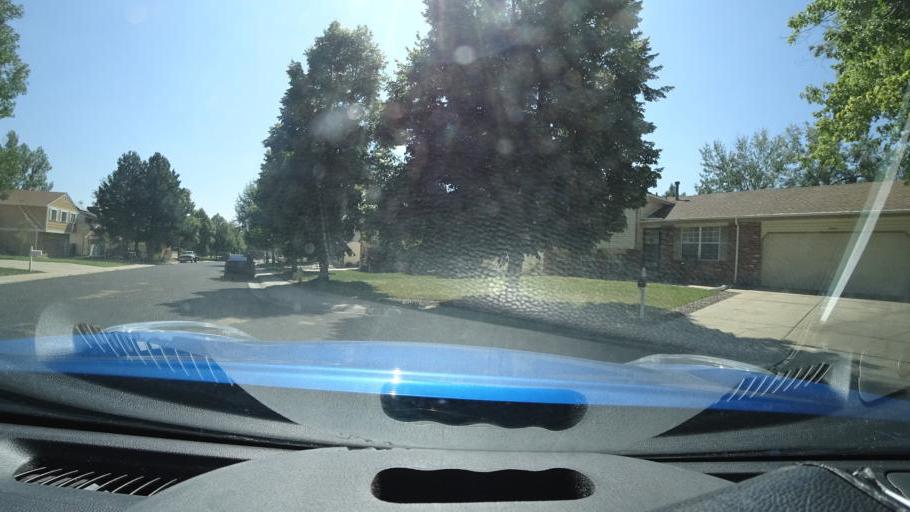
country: US
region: Colorado
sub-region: Adams County
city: Aurora
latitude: 39.6768
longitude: -104.8210
